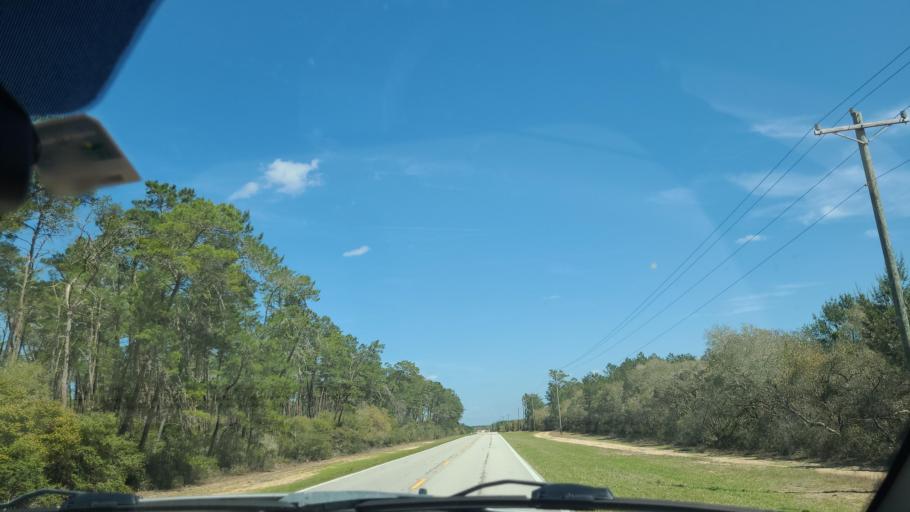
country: US
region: Florida
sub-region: Marion County
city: Citra
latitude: 29.3680
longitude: -81.8561
